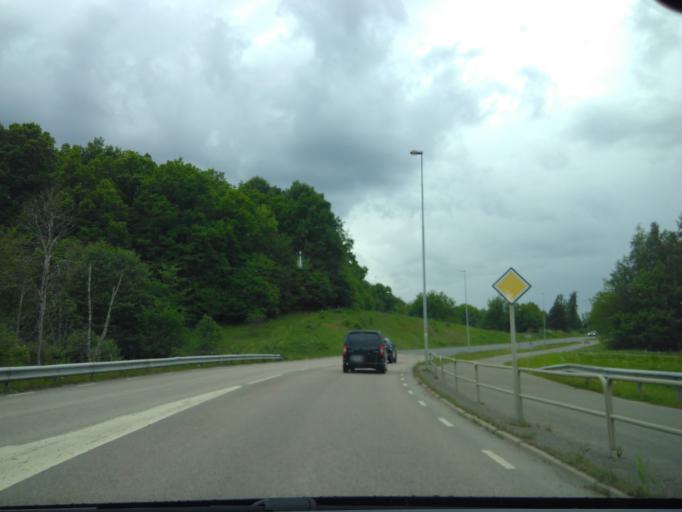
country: SE
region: Vaestra Goetaland
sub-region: Skovde Kommun
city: Skoevde
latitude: 58.4124
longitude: 13.8452
